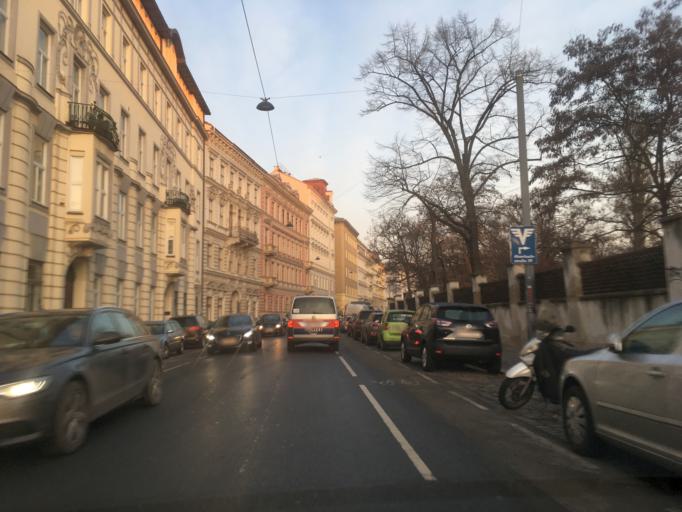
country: AT
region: Vienna
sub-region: Wien Stadt
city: Vienna
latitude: 48.2228
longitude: 16.3583
